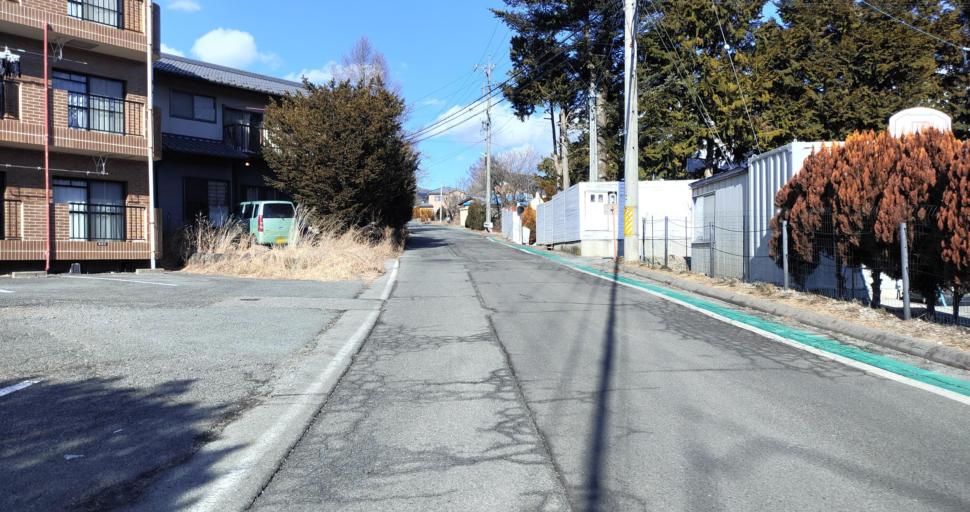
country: JP
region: Nagano
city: Komoro
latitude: 36.3324
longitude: 138.5114
